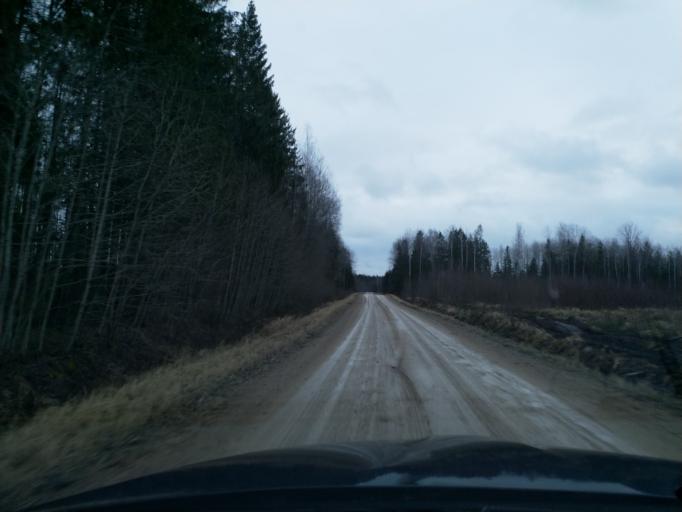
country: LV
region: Kuldigas Rajons
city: Kuldiga
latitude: 56.9267
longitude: 22.2583
